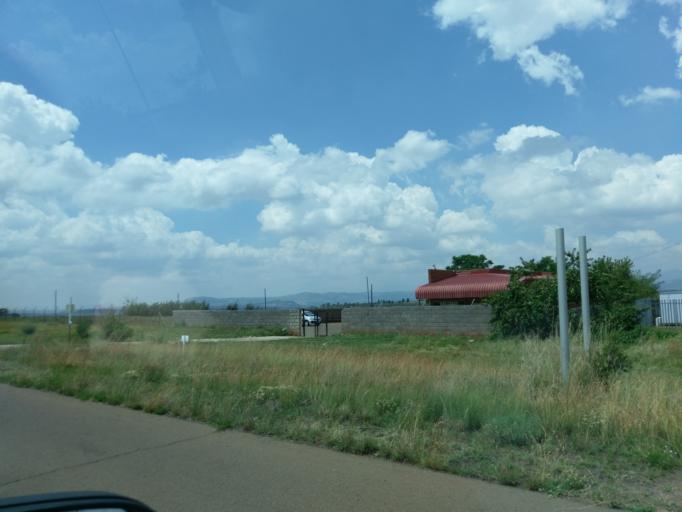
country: LS
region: Maseru
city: Maseru
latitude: -29.4584
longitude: 27.5596
